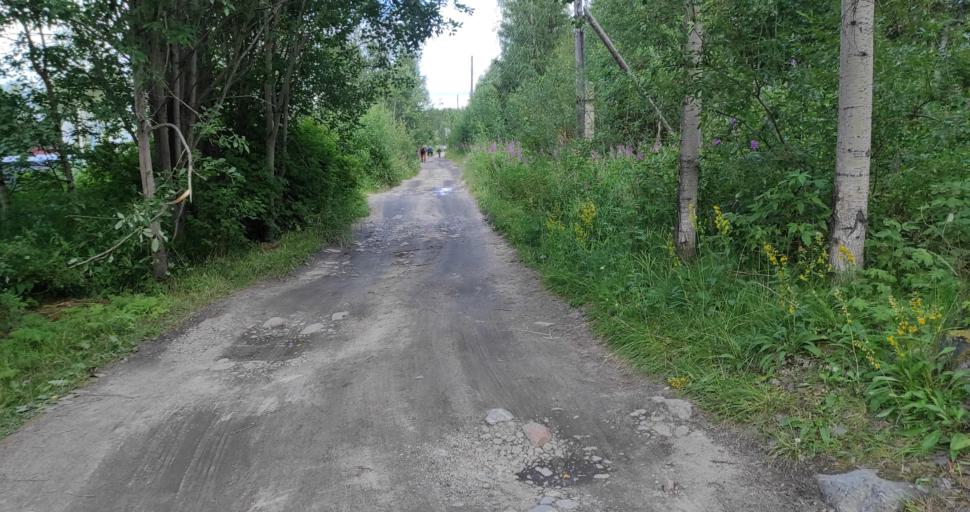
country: RU
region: Murmansk
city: Afrikanda
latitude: 67.0813
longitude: 32.9874
